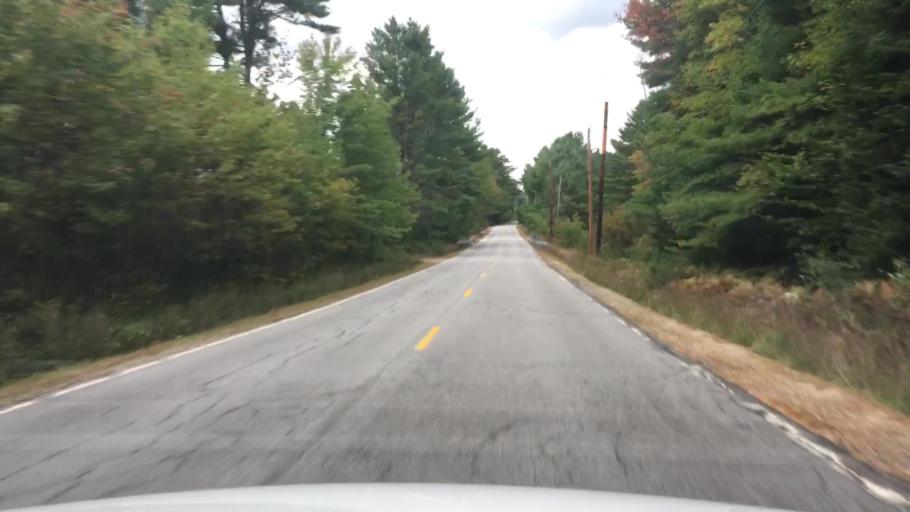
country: US
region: Maine
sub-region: York County
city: Parsonsfield
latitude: 43.7053
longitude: -70.9819
